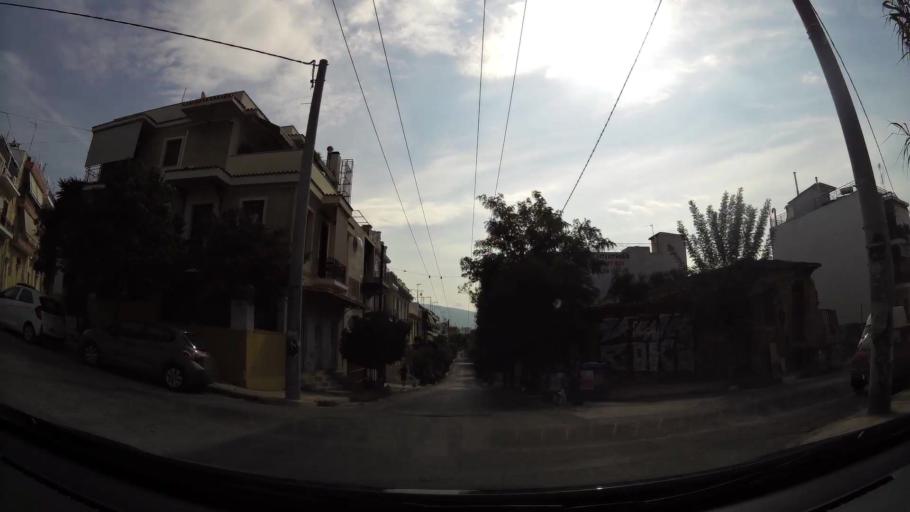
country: GR
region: Attica
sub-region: Nomarchia Athinas
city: Athens
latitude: 37.9663
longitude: 23.7140
